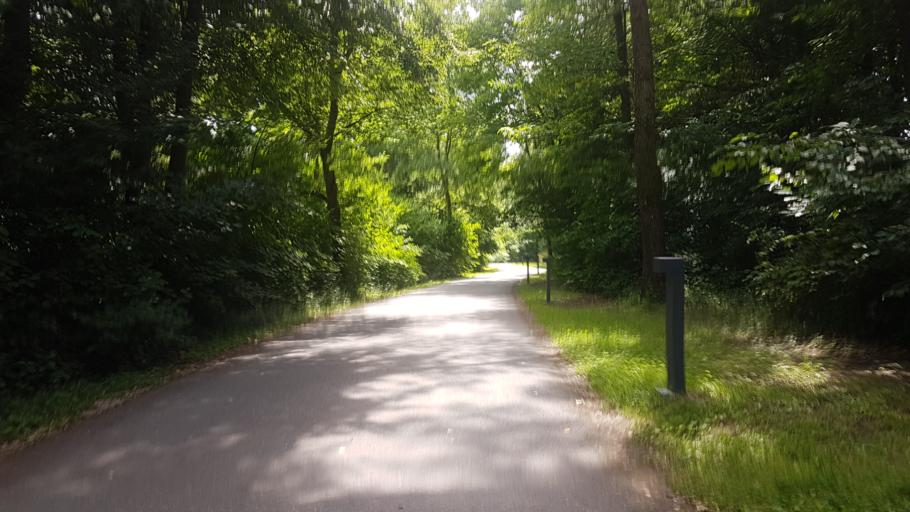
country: DE
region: Bavaria
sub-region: Regierungsbezirk Mittelfranken
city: Absberg
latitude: 49.1287
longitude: 10.8678
